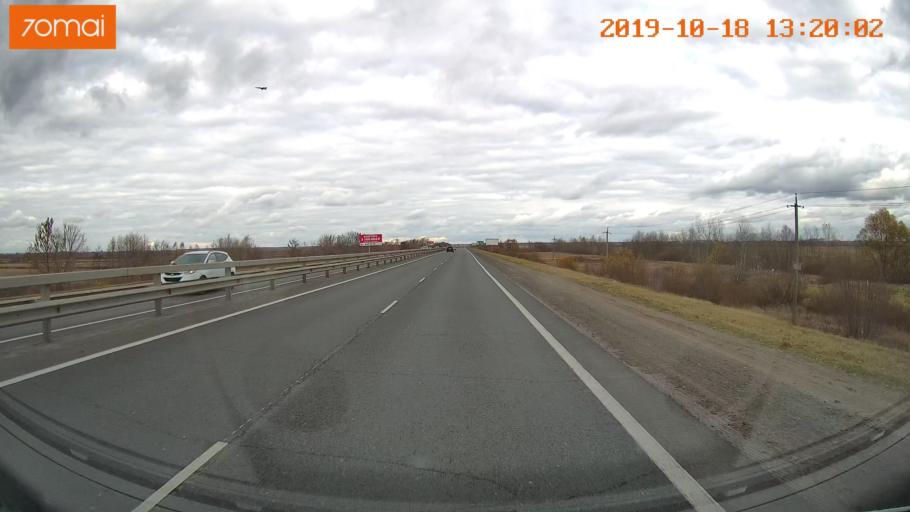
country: RU
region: Rjazan
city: Polyany
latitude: 54.6750
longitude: 39.8291
